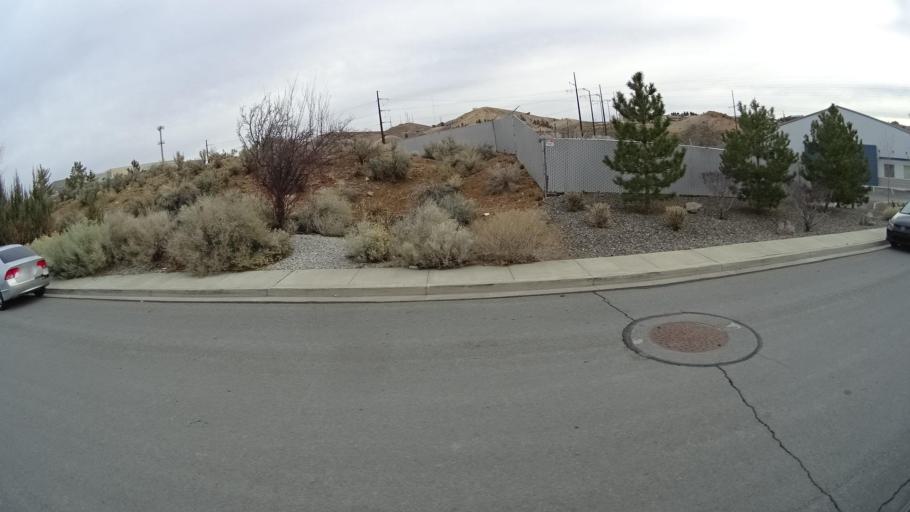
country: US
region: Nevada
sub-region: Washoe County
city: Reno
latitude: 39.5689
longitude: -119.8086
